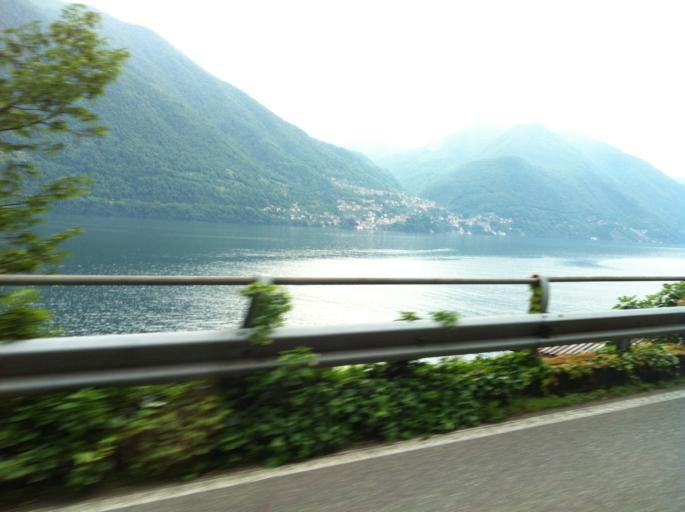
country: IT
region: Lombardy
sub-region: Provincia di Como
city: Argegno
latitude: 45.9320
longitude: 9.1283
